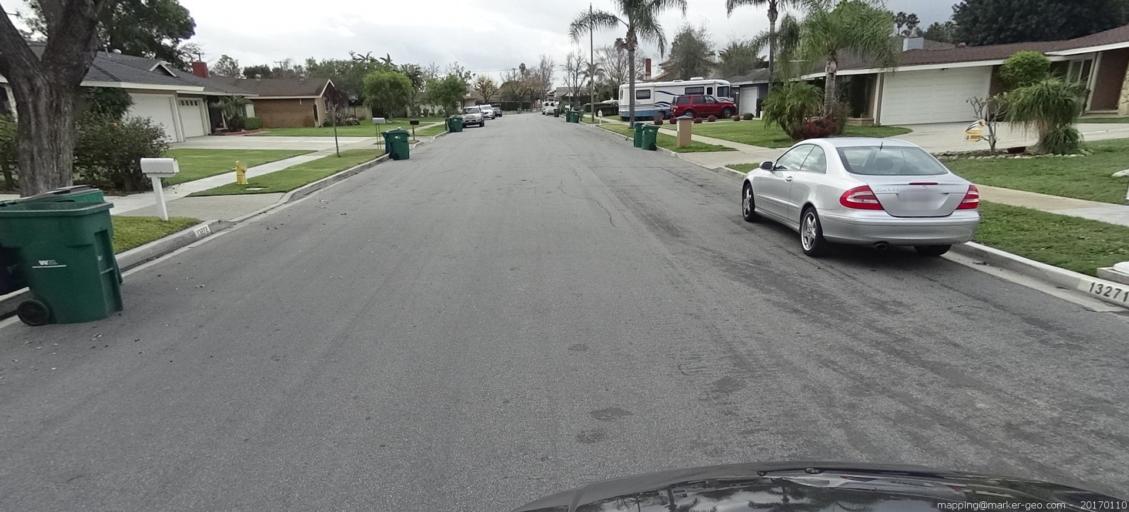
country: US
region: California
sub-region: Orange County
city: Tustin
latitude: 33.7695
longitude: -117.8281
